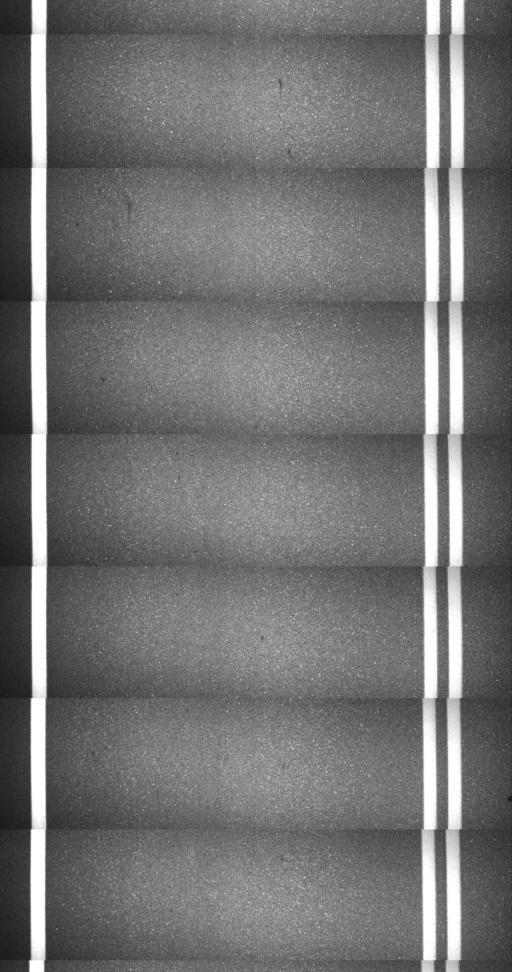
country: US
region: Vermont
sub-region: Windham County
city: Dover
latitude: 43.0280
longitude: -72.8317
